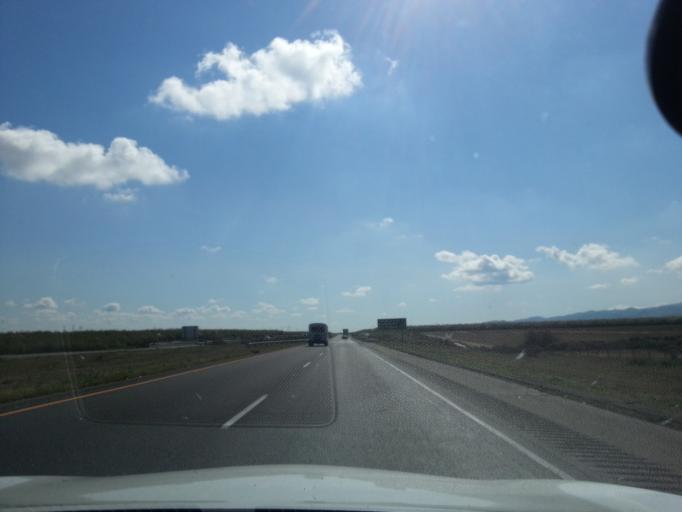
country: US
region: California
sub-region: Fresno County
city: San Joaquin
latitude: 36.4196
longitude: -120.3800
